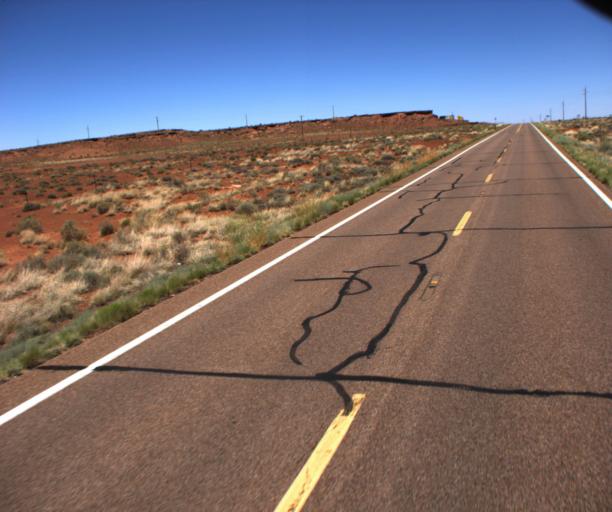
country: US
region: Arizona
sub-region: Coconino County
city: LeChee
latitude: 34.9277
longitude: -110.8040
